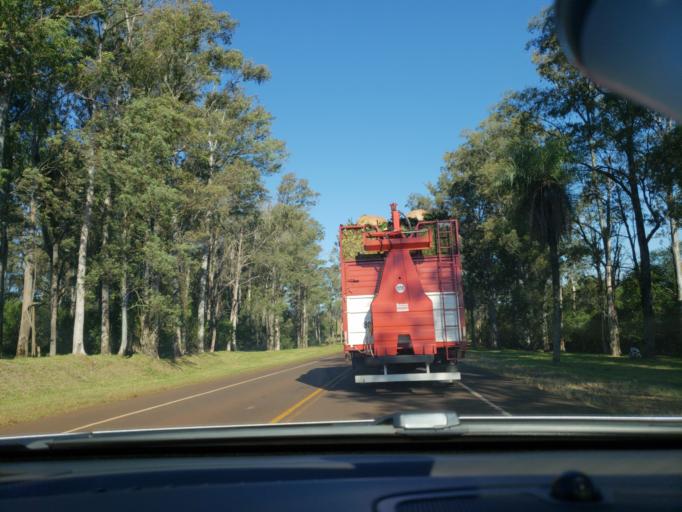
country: AR
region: Misiones
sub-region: Departamento de Apostoles
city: San Jose
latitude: -27.8337
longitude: -55.7695
